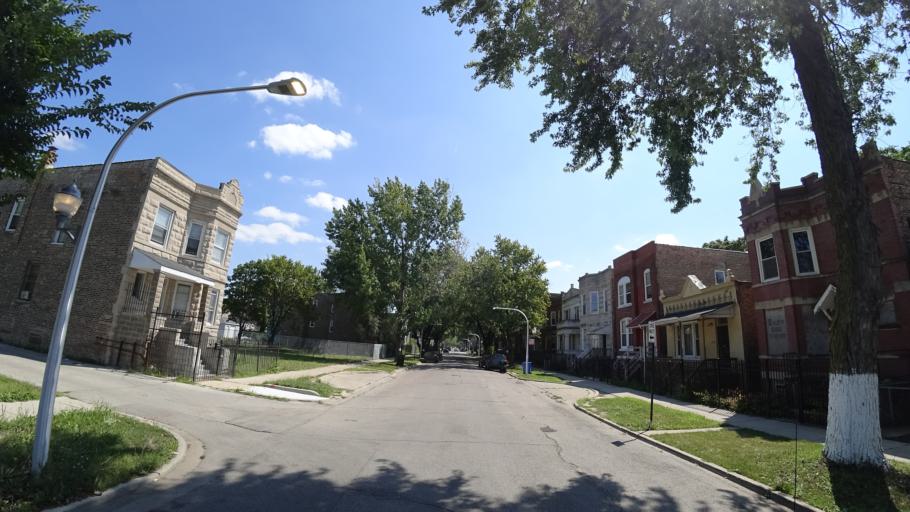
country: US
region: Illinois
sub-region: Cook County
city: Cicero
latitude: 41.8671
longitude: -87.7247
